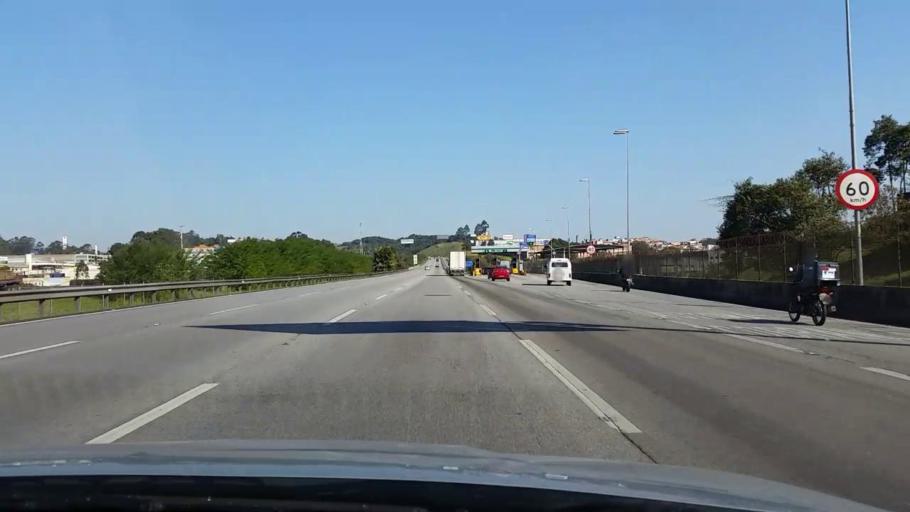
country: BR
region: Sao Paulo
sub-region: Diadema
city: Diadema
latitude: -23.7164
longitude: -46.6054
